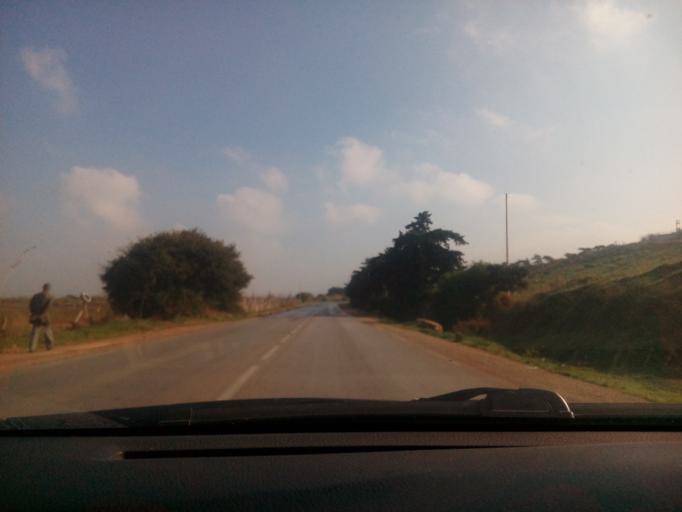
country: DZ
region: Oran
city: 'Ain el Turk
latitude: 35.7045
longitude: -0.8300
